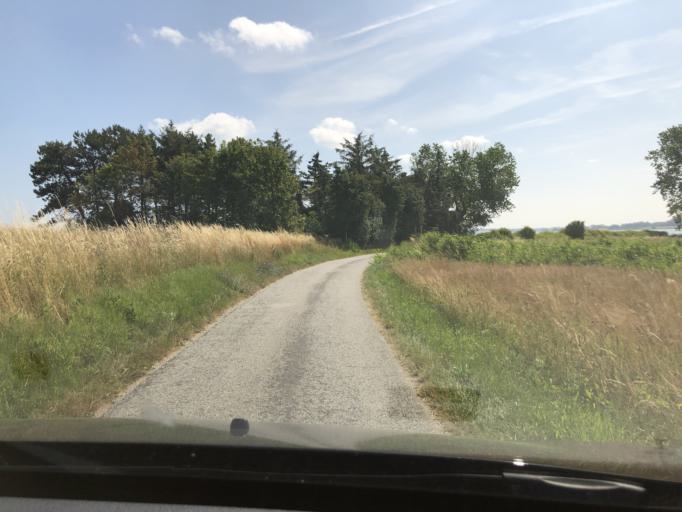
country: DK
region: South Denmark
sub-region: AEro Kommune
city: AEroskobing
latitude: 54.9130
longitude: 10.3236
